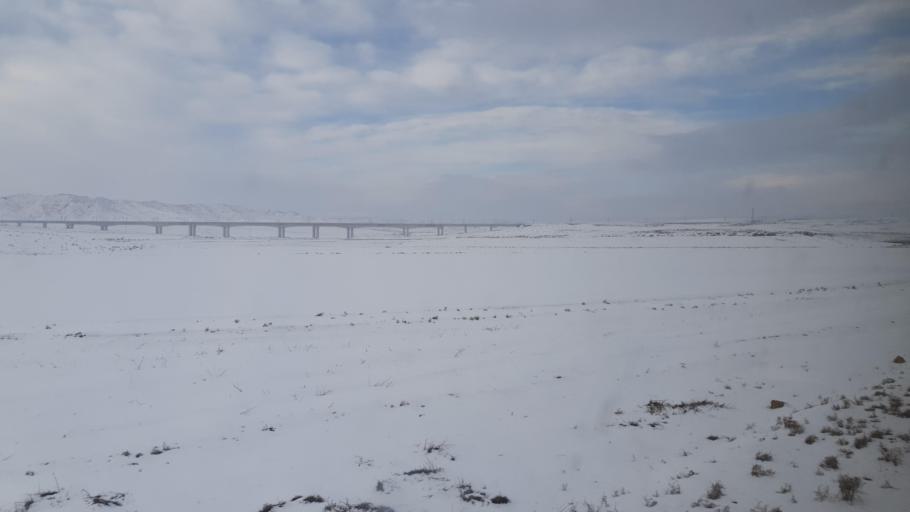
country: TR
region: Kirikkale
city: Delice
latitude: 39.8948
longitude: 33.9878
